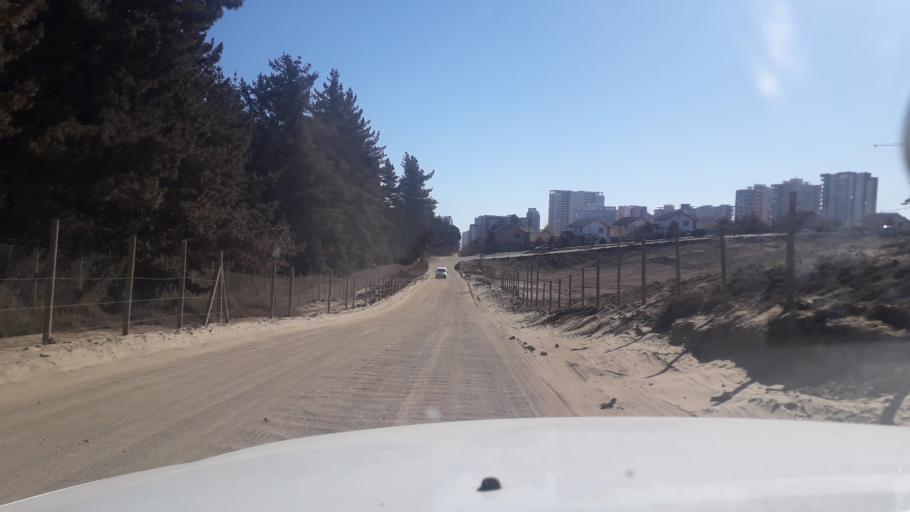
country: CL
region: Valparaiso
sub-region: Provincia de Valparaiso
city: Vina del Mar
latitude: -32.9530
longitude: -71.5323
